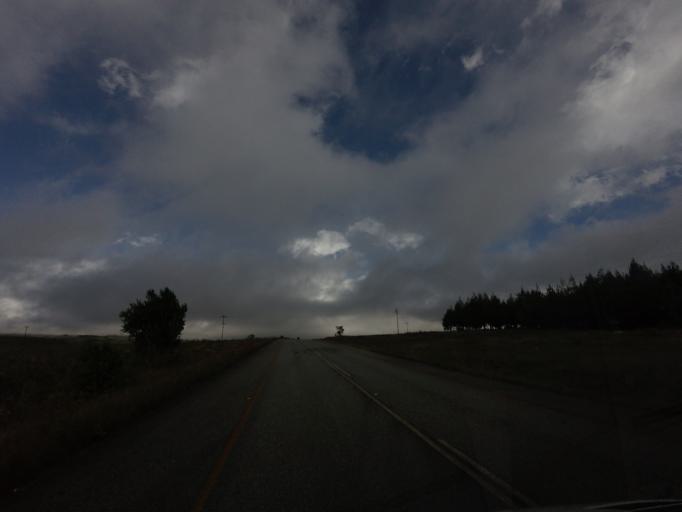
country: ZA
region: Mpumalanga
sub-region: Ehlanzeni District
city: Graksop
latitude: -24.8560
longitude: 30.8760
